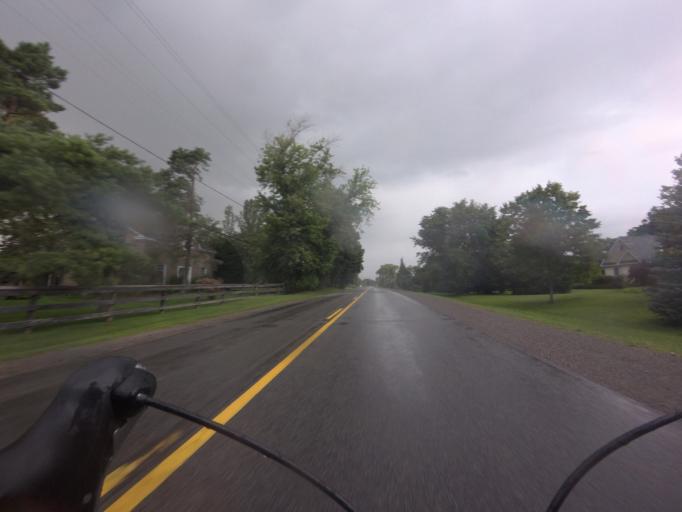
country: CA
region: Ontario
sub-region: Lanark County
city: Smiths Falls
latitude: 44.9361
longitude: -75.8305
